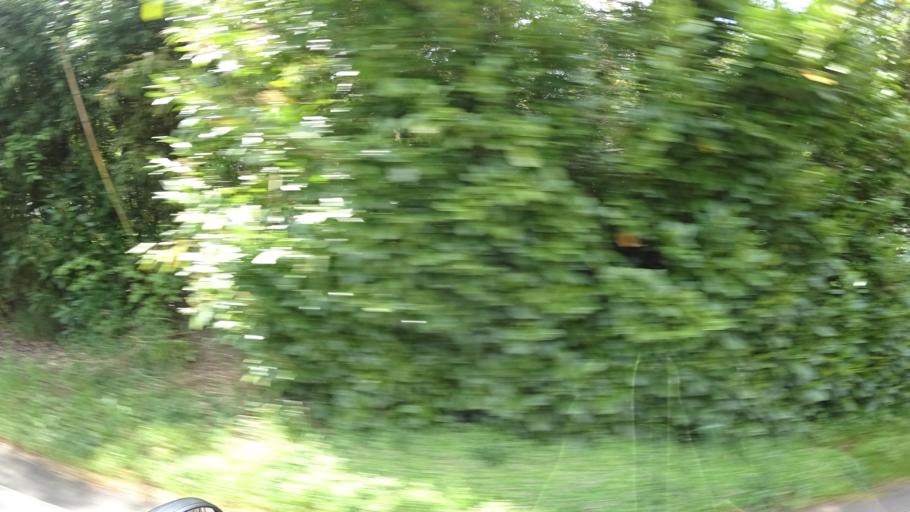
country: US
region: Oregon
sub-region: Washington County
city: Hillsboro
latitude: 45.5398
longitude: -122.9986
